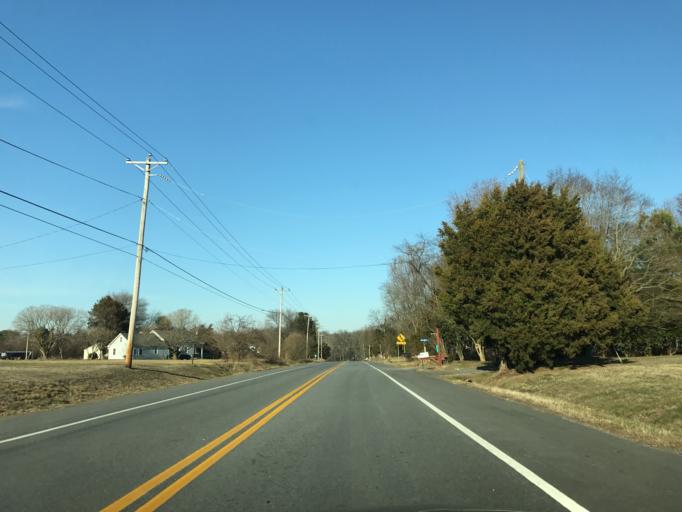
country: US
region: Maryland
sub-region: Queen Anne's County
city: Kingstown
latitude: 39.2461
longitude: -75.8644
